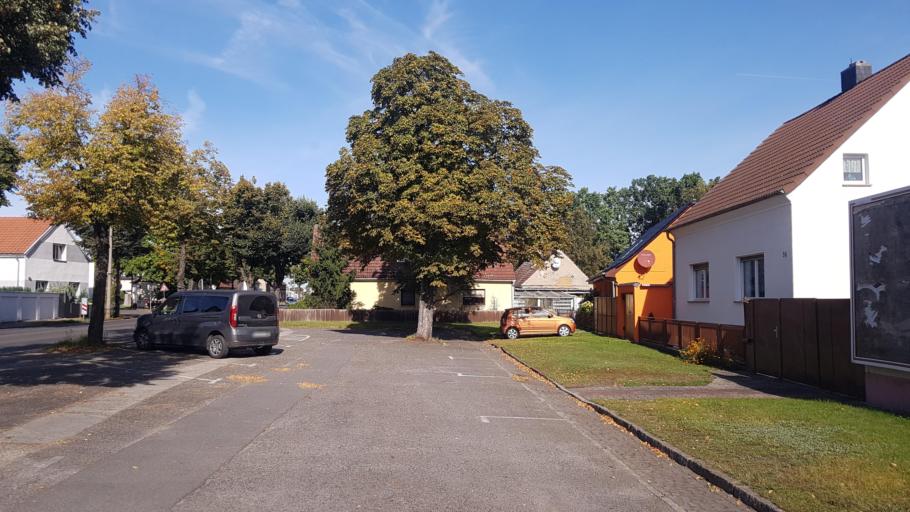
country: DE
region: Brandenburg
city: Lauchhammer
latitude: 51.4729
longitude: 13.7380
